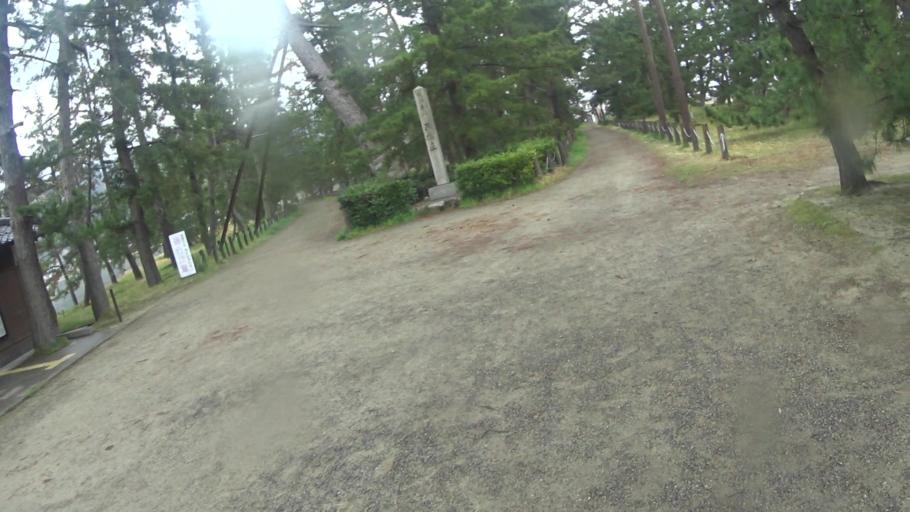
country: JP
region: Kyoto
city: Miyazu
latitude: 35.5769
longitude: 135.1979
